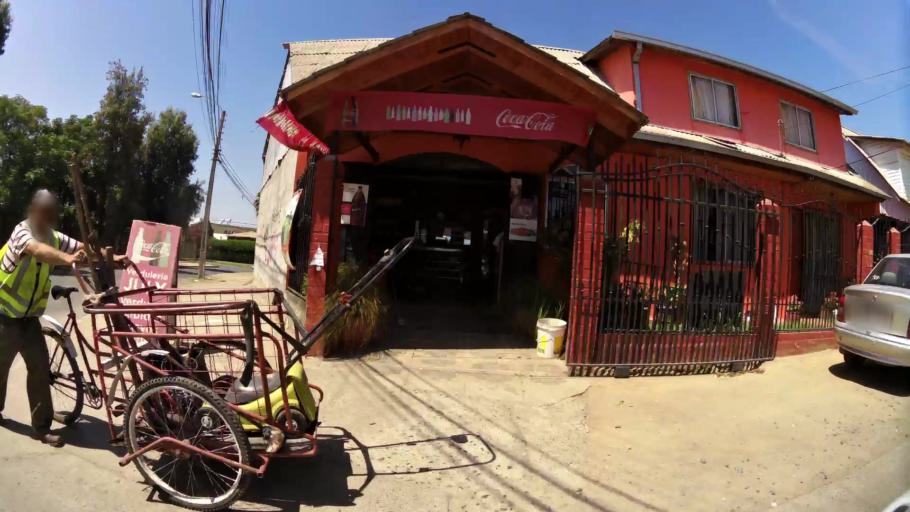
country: CL
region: Maule
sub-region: Provincia de Talca
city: Talca
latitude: -35.4242
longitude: -71.6273
